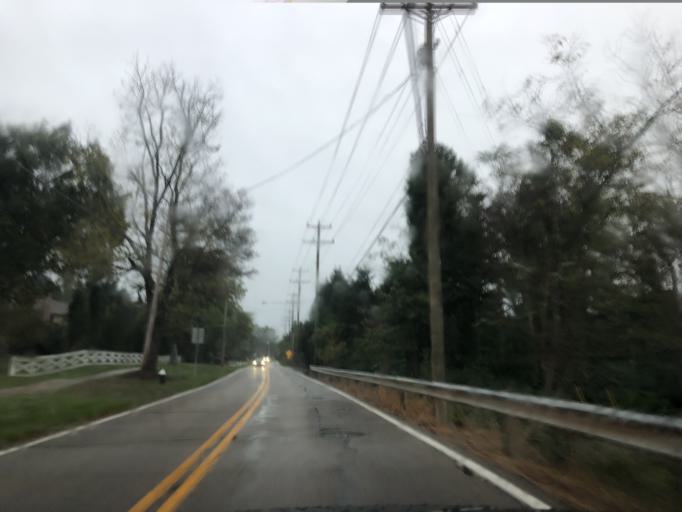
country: US
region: Ohio
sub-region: Hamilton County
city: The Village of Indian Hill
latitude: 39.2342
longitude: -84.3167
